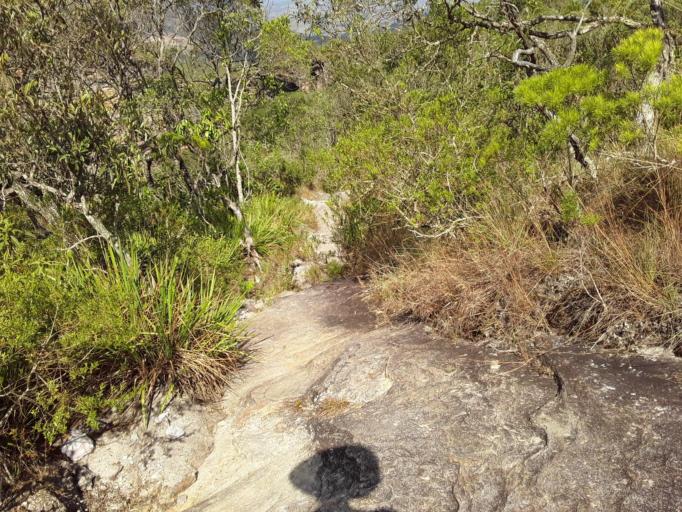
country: BR
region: Minas Gerais
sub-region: Lima Duarte
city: Lima Duarte
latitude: -21.7125
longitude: -43.8944
